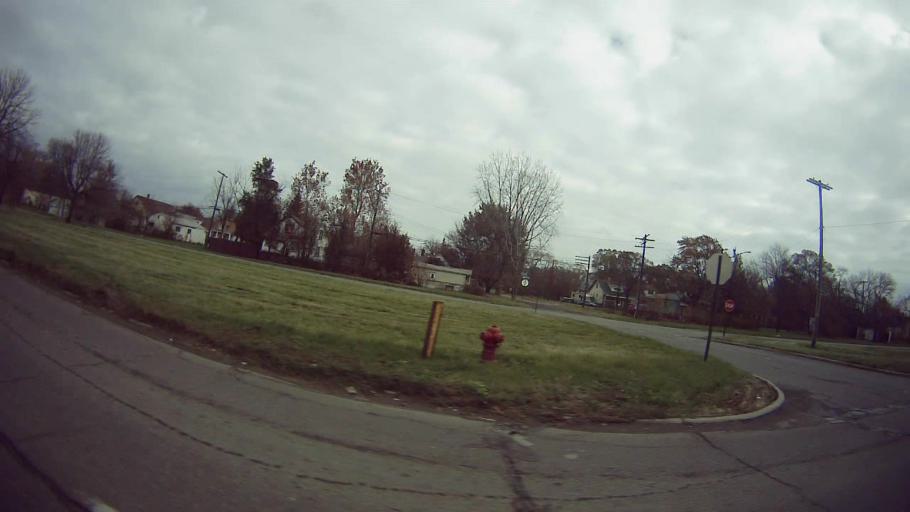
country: US
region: Michigan
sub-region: Wayne County
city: Hamtramck
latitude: 42.4249
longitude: -83.0434
